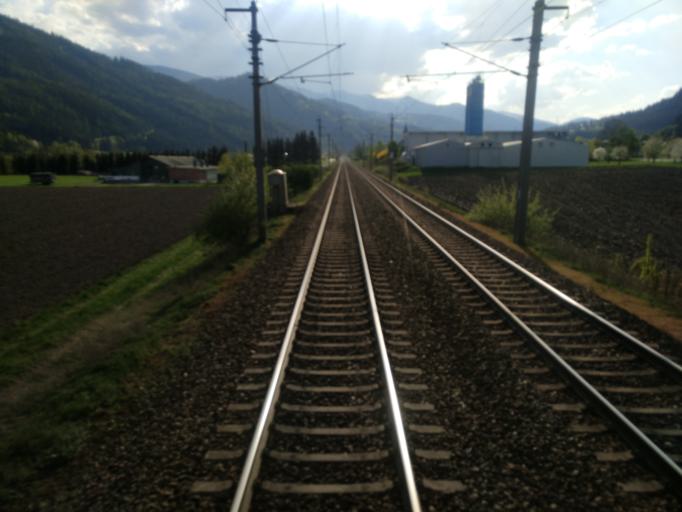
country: AT
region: Styria
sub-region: Politischer Bezirk Leoben
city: Kammern im Liesingtal
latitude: 47.3919
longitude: 14.9123
